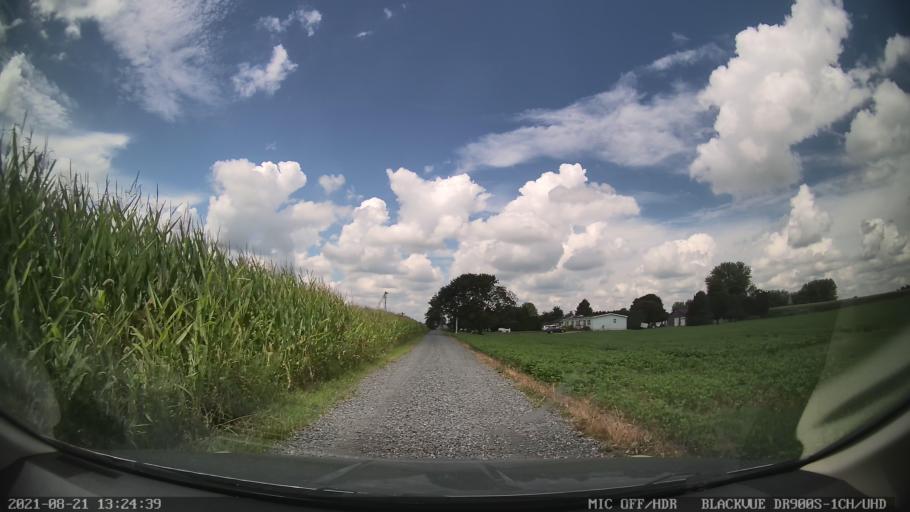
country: US
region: Pennsylvania
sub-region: Berks County
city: Fleetwood
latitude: 40.4726
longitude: -75.7820
